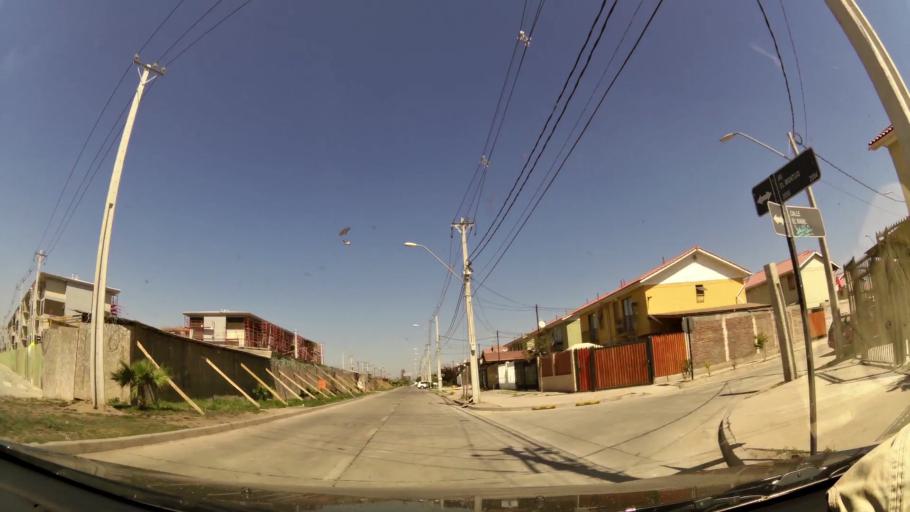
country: CL
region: Santiago Metropolitan
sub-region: Provincia de Santiago
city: Lo Prado
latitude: -33.3931
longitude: -70.7531
